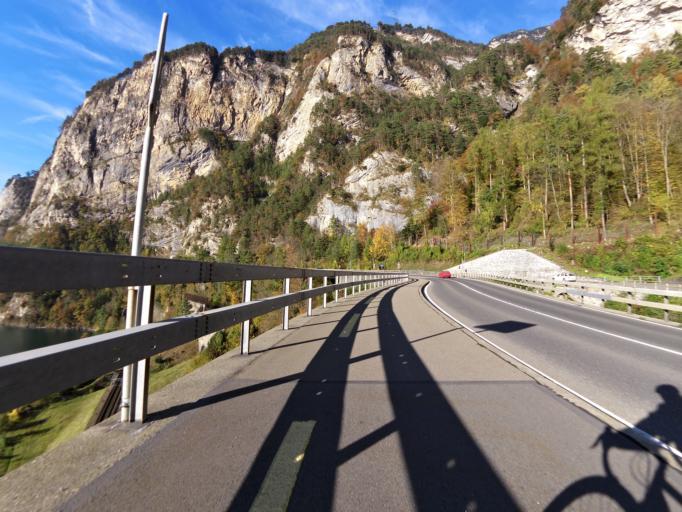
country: CH
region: Uri
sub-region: Uri
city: Flueelen
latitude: 46.9192
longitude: 8.6227
